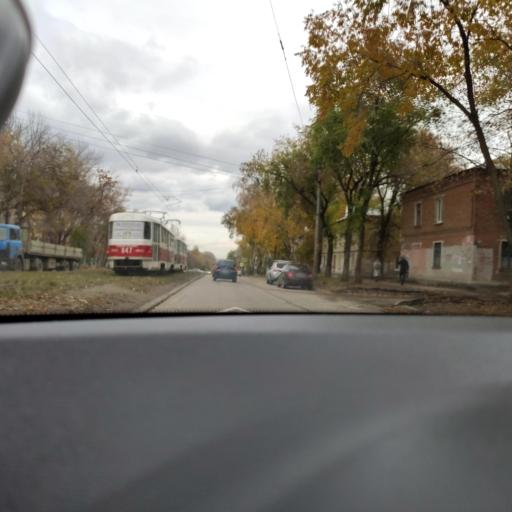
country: RU
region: Samara
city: Samara
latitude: 53.2203
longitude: 50.2288
